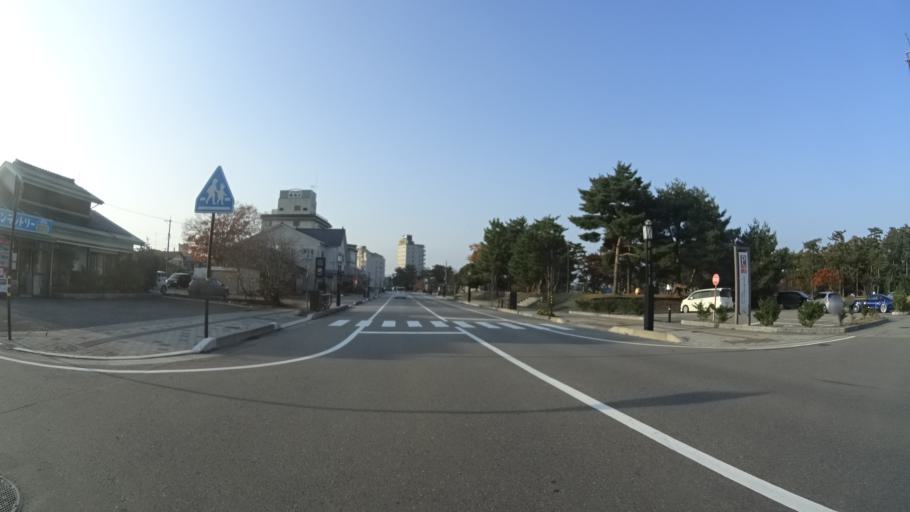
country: JP
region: Ishikawa
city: Nanao
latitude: 37.0861
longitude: 136.9246
